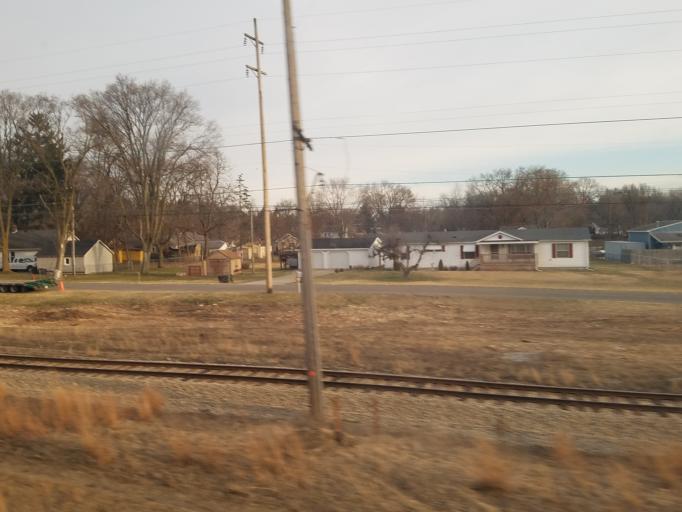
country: US
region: Indiana
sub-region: Saint Joseph County
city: South Bend
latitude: 41.6849
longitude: -86.3211
